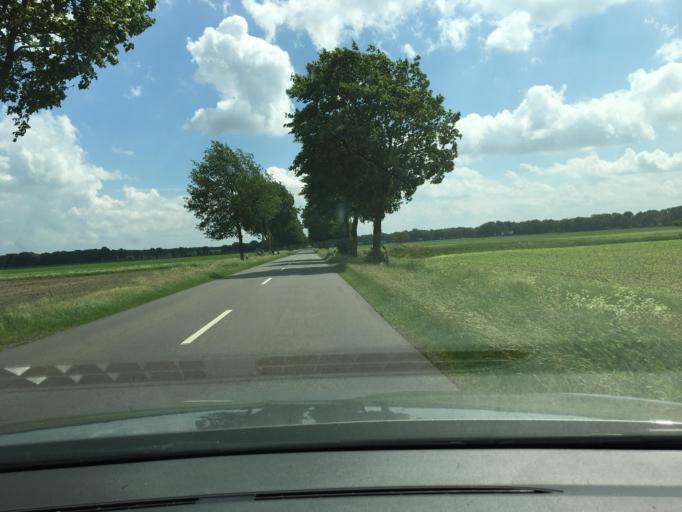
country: DE
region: Lower Saxony
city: Tarmstedt
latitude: 53.2359
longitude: 9.0475
